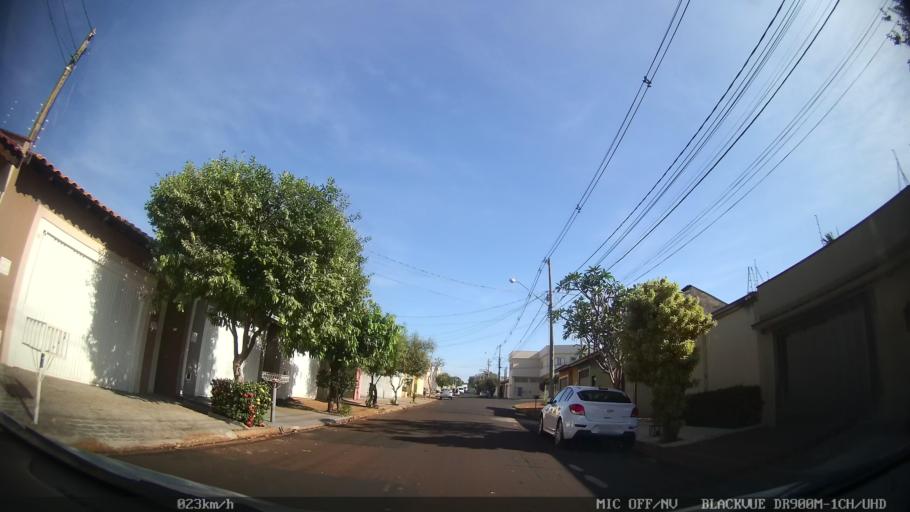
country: BR
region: Sao Paulo
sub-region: Ribeirao Preto
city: Ribeirao Preto
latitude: -21.1764
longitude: -47.7613
